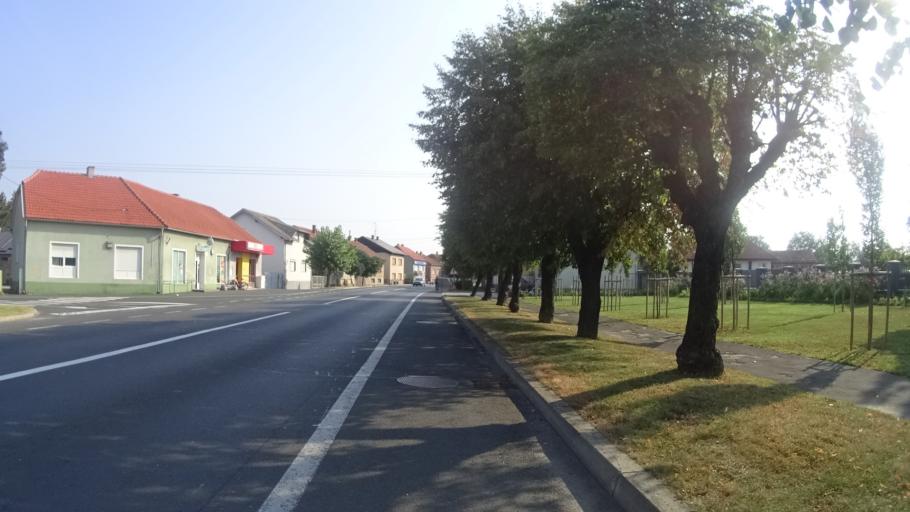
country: HR
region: Medimurska
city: Nedelisce
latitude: 46.3773
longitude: 16.3907
